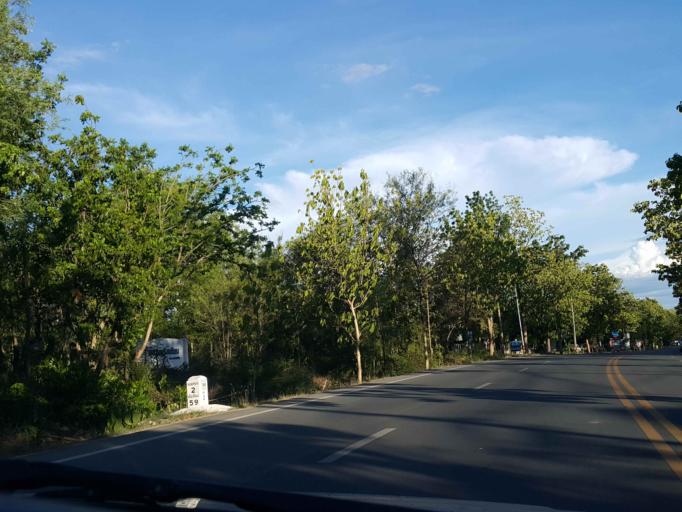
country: TH
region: Chiang Mai
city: Chom Thong
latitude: 18.4482
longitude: 98.6756
